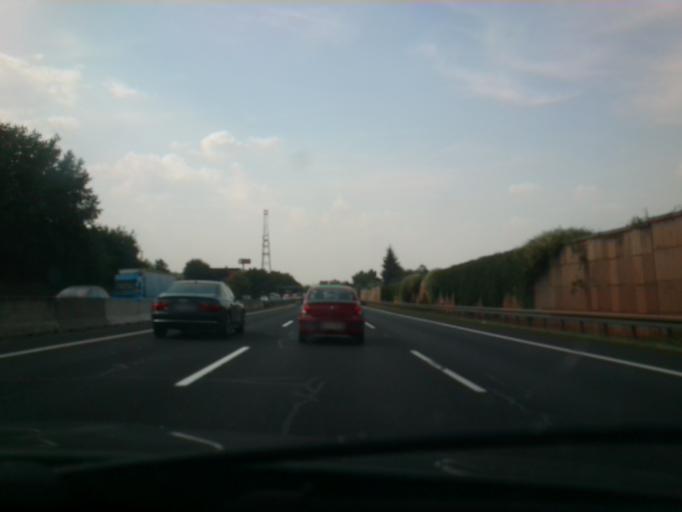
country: CZ
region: Central Bohemia
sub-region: Okres Praha-Vychod
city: Ricany
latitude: 49.9610
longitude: 14.6304
